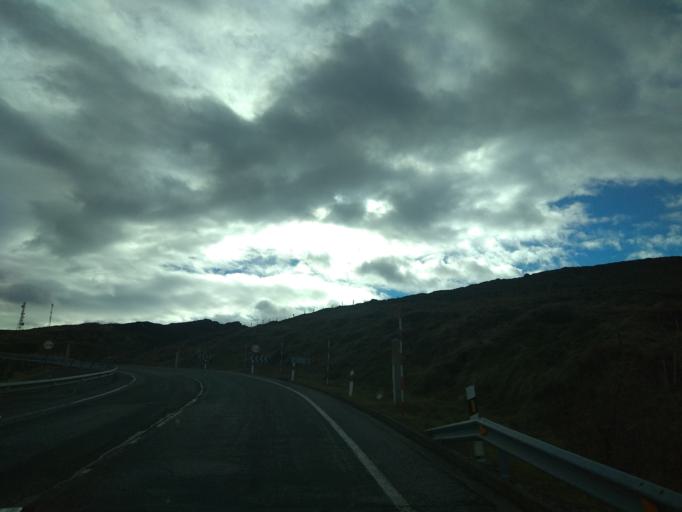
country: ES
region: Castille and Leon
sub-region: Provincia de Burgos
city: Arija
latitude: 43.0556
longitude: -3.8866
